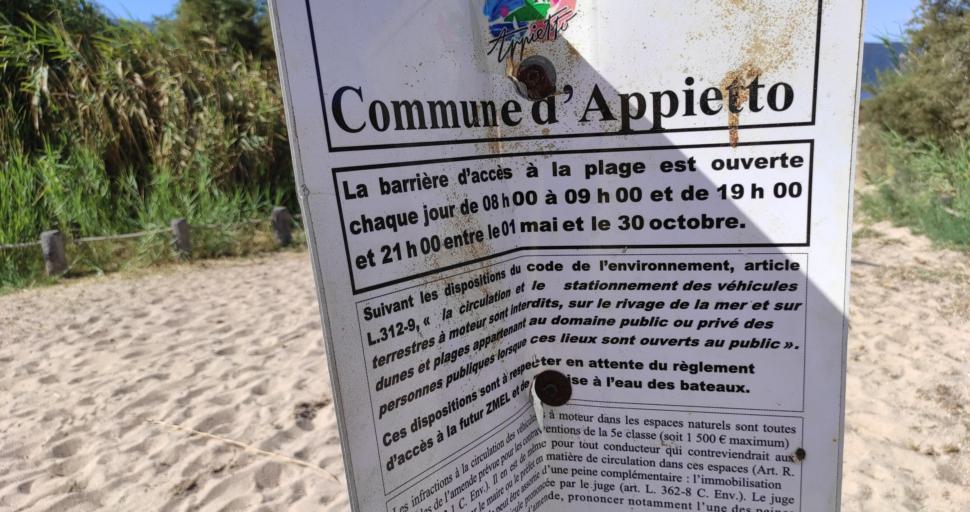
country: FR
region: Corsica
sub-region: Departement de la Corse-du-Sud
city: Alata
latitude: 41.9934
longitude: 8.6684
